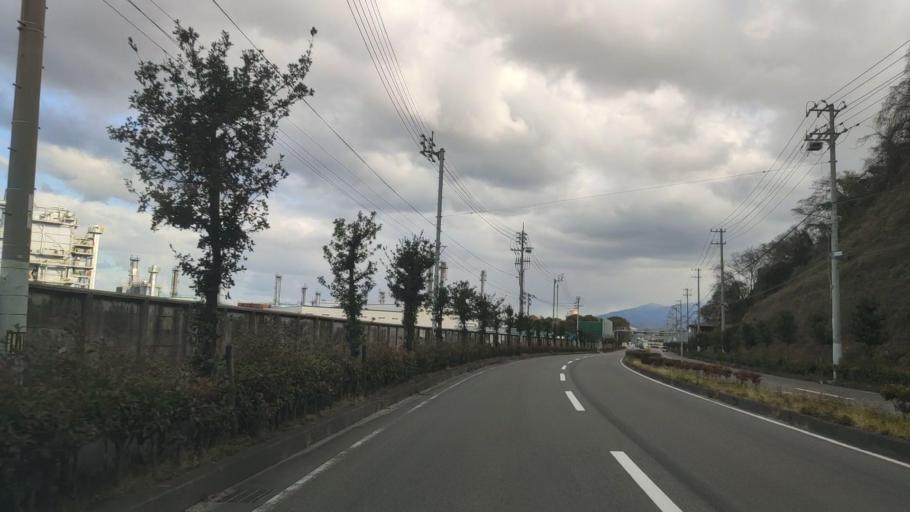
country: JP
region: Ehime
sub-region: Shikoku-chuo Shi
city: Matsuyama
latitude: 33.8449
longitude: 132.7088
